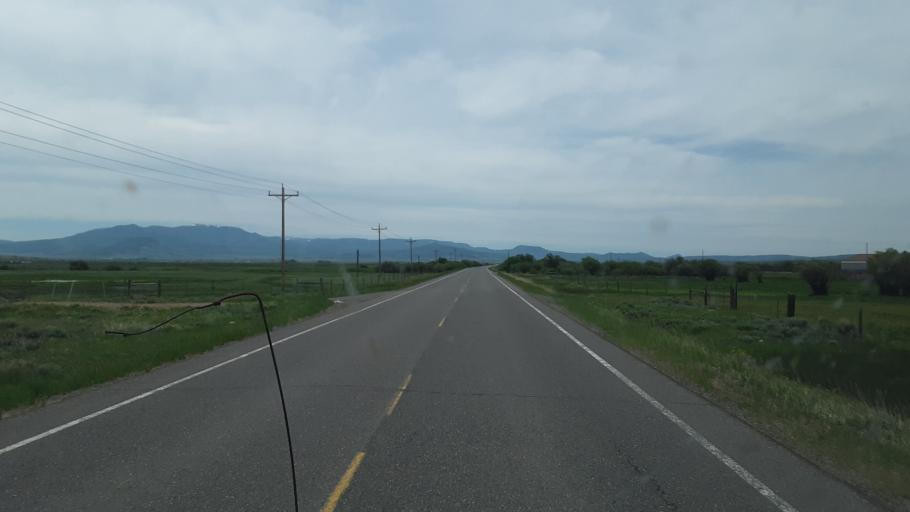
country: US
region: Colorado
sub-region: Jackson County
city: Walden
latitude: 40.5741
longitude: -106.4071
